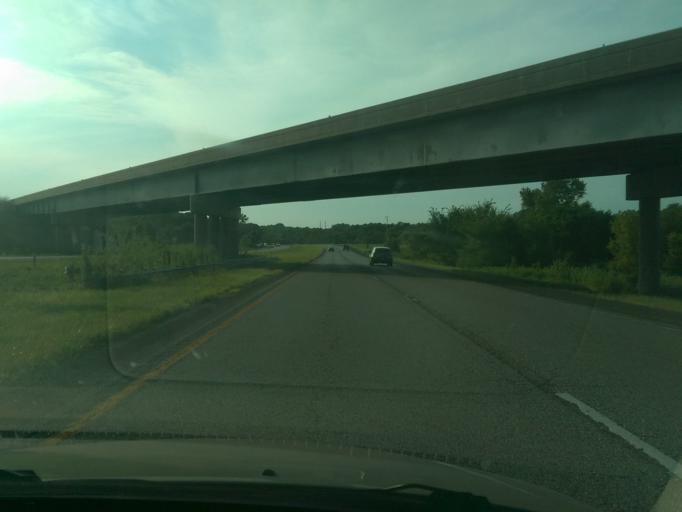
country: US
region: Missouri
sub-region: Platte County
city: Weatherby Lake
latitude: 39.3185
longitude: -94.6940
